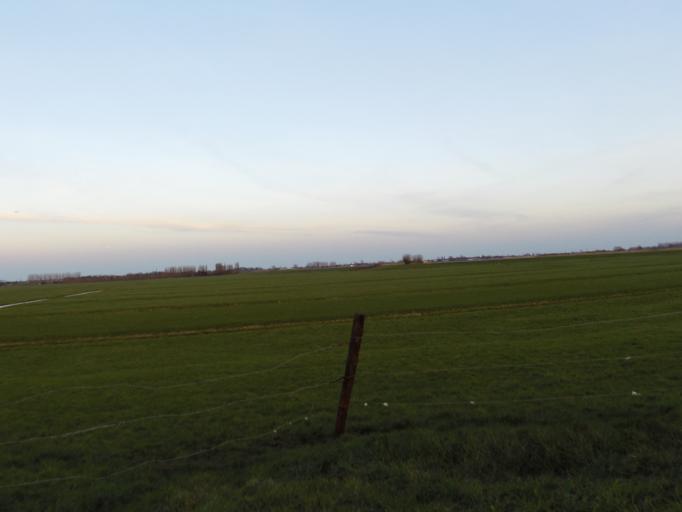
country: NL
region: South Holland
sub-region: Gemeente Kaag en Braassem
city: Oude Wetering
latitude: 52.1734
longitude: 4.5996
